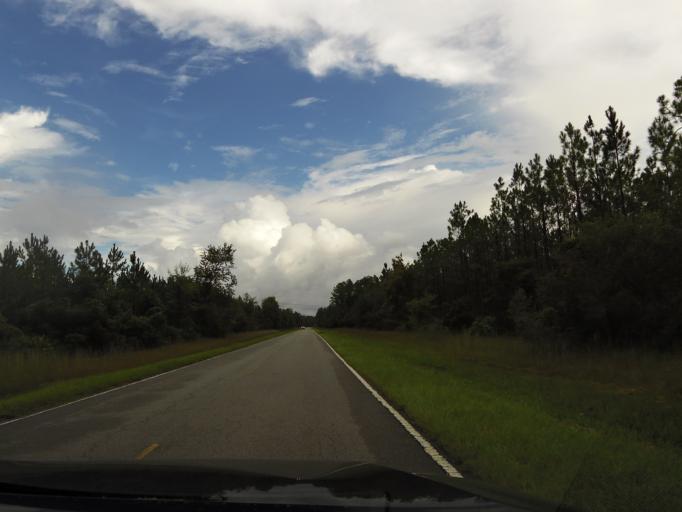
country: US
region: Florida
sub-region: Duval County
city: Baldwin
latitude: 30.3977
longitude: -81.9562
